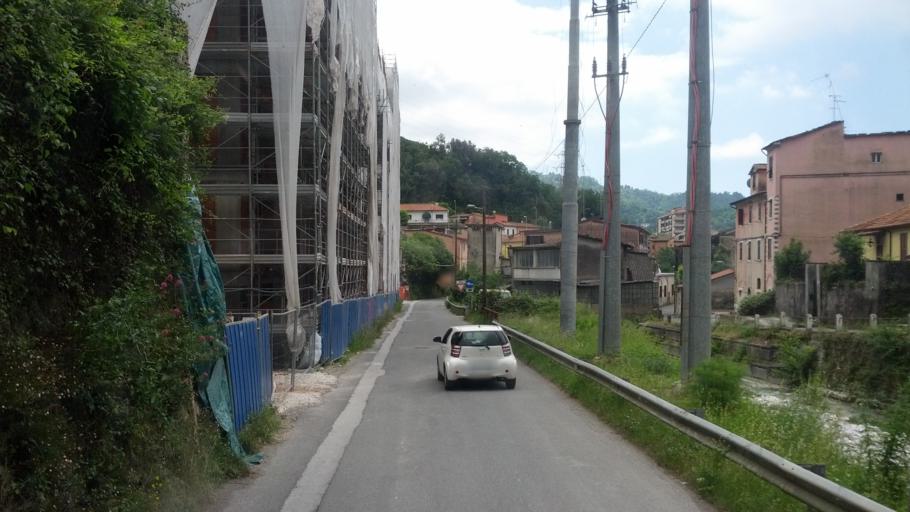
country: IT
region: Tuscany
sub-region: Provincia di Massa-Carrara
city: Carrara
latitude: 44.0837
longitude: 10.1033
